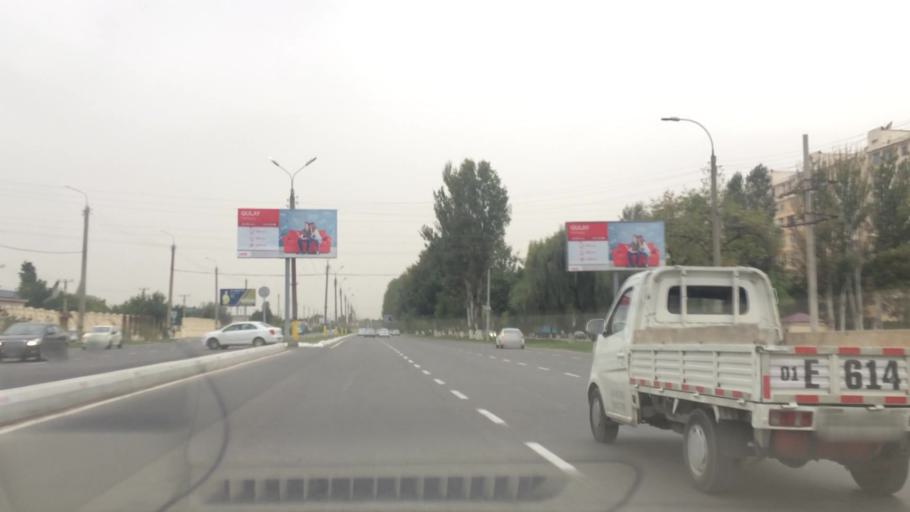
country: UZ
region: Toshkent
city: Salor
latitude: 41.3199
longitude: 69.3603
